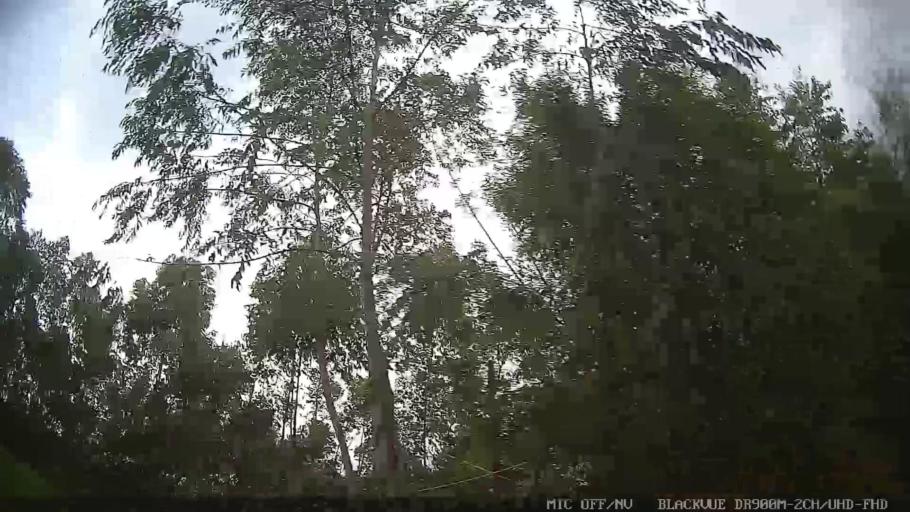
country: BR
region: Sao Paulo
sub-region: Itatiba
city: Itatiba
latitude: -22.9358
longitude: -46.7948
